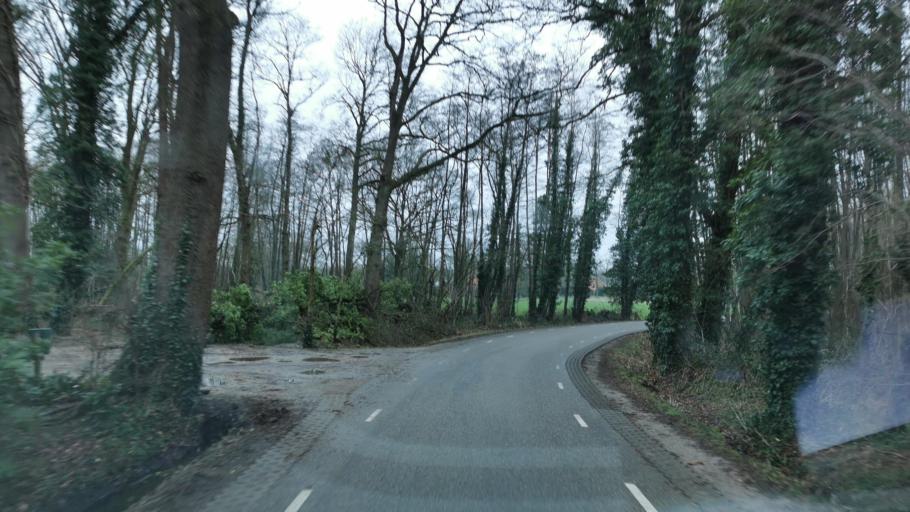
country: NL
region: Overijssel
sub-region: Gemeente Hengelo
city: Hengelo
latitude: 52.3307
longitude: 6.8177
